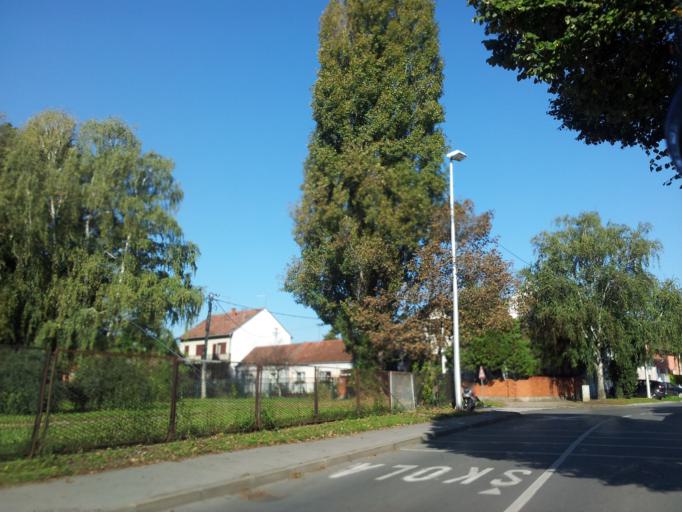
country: HR
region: Osjecko-Baranjska
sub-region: Grad Osijek
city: Osijek
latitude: 45.5480
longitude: 18.7141
